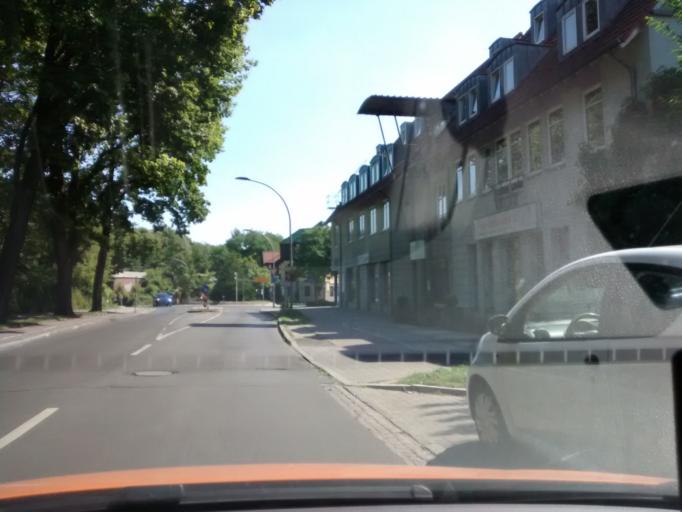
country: DE
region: Brandenburg
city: Hohen Neuendorf
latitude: 52.6632
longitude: 13.2852
